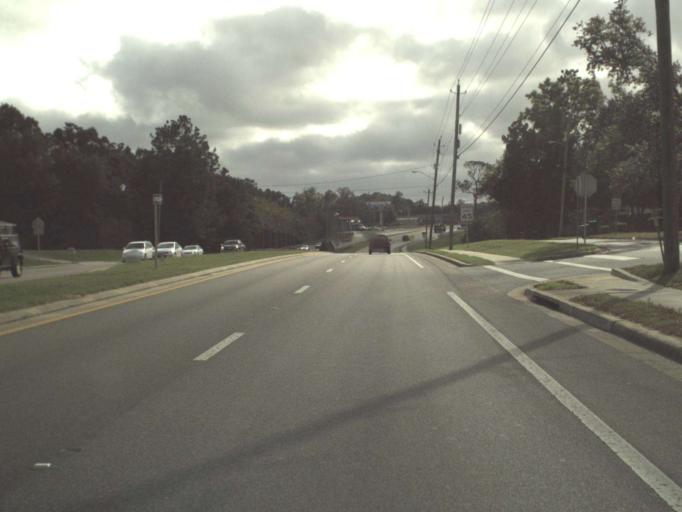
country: US
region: Florida
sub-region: Santa Rosa County
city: Milton
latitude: 30.6305
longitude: -87.0559
